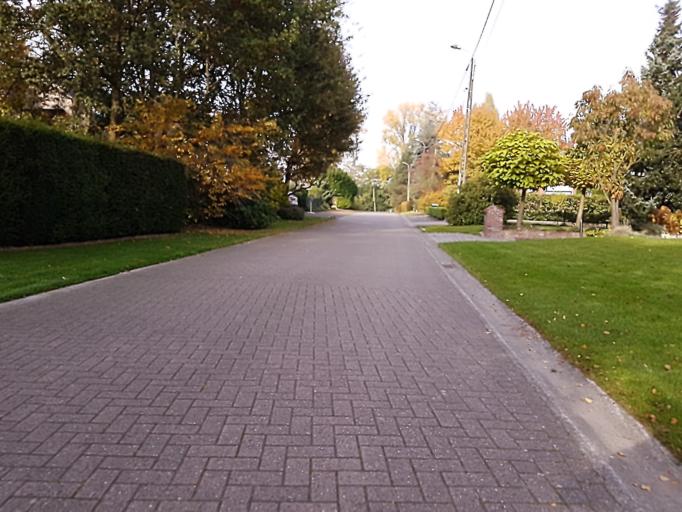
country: BE
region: Flanders
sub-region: Provincie Antwerpen
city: Sint-Katelijne-Waver
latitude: 51.0598
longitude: 4.5176
